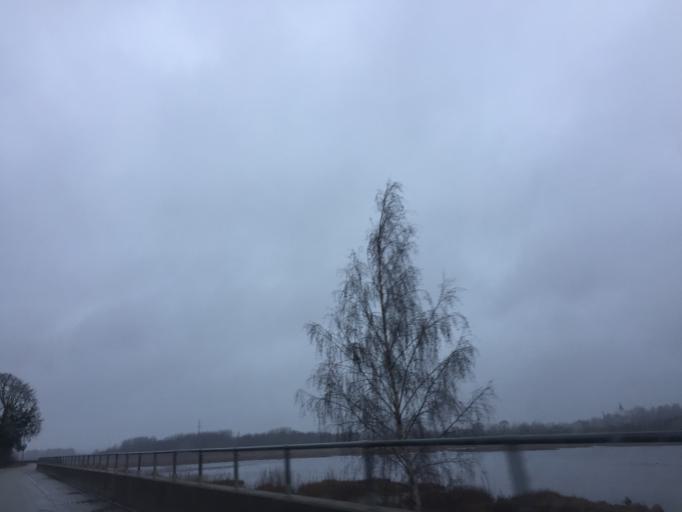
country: LV
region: Jekabpils Rajons
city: Jekabpils
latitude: 56.5041
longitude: 25.8544
